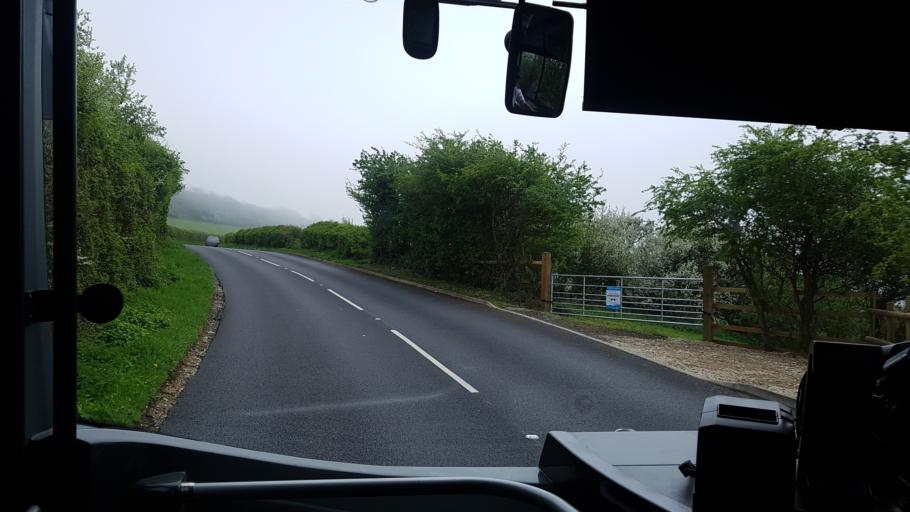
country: GB
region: England
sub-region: Isle of Wight
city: Ventnor
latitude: 50.6089
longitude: -1.2249
